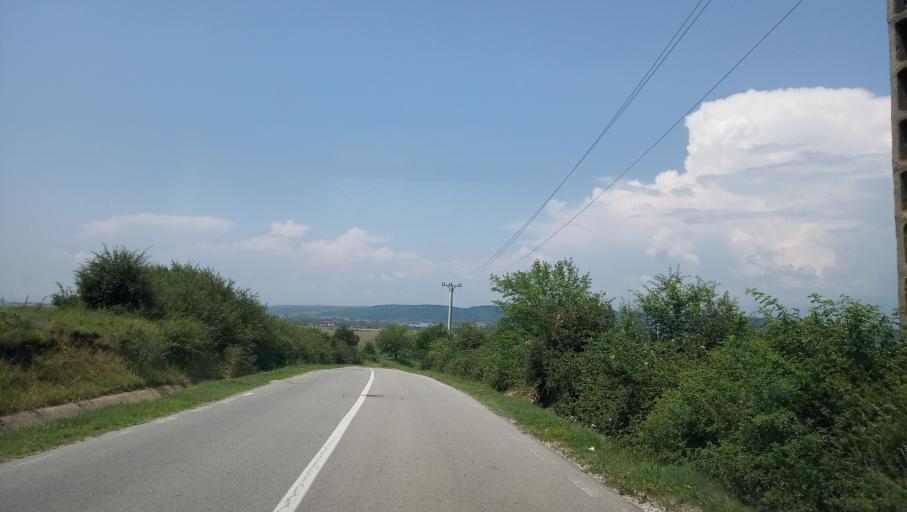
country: RO
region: Gorj
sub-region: Comuna Turcinesti
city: Turcinesti
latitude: 45.0639
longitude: 23.3281
